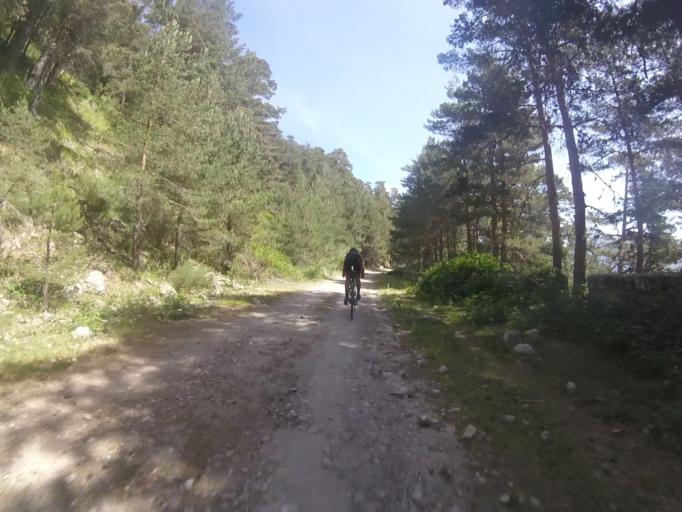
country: ES
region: Madrid
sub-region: Provincia de Madrid
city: Cercedilla
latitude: 40.7998
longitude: -4.0600
